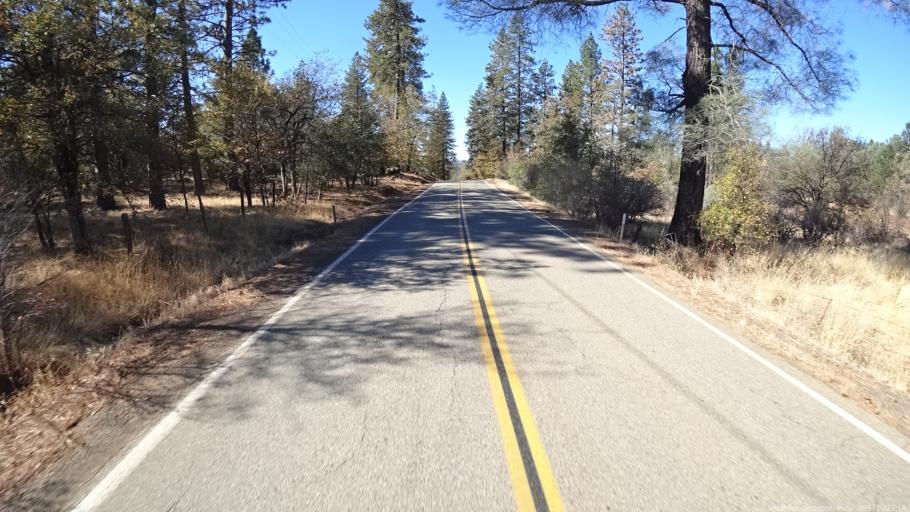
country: US
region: California
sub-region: Shasta County
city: Bella Vista
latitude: 40.6849
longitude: -122.0341
